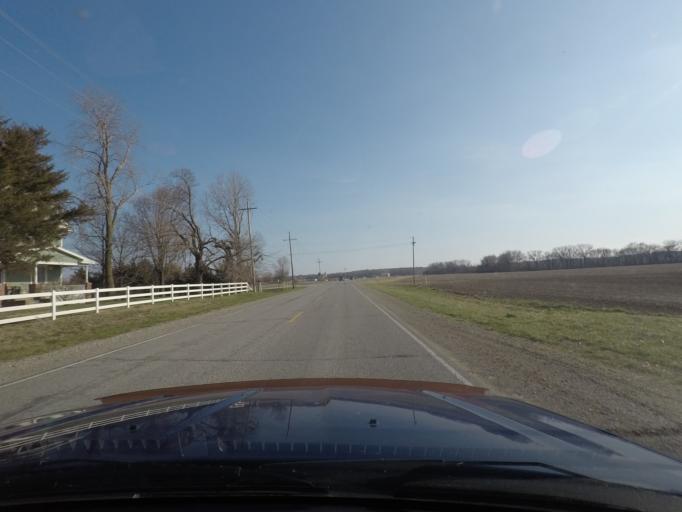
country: US
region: Kansas
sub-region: Jefferson County
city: Oskaloosa
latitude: 39.0632
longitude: -95.3819
